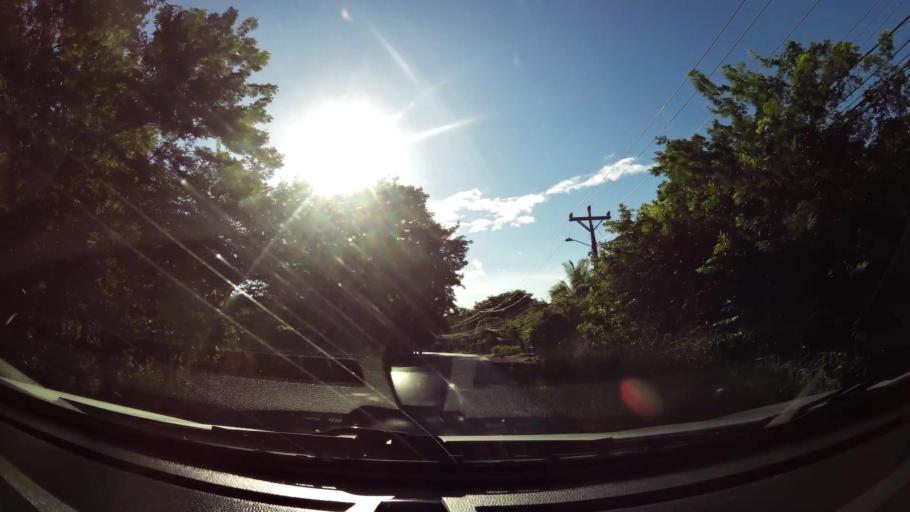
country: CR
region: Guanacaste
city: Sardinal
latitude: 10.5243
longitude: -85.6527
